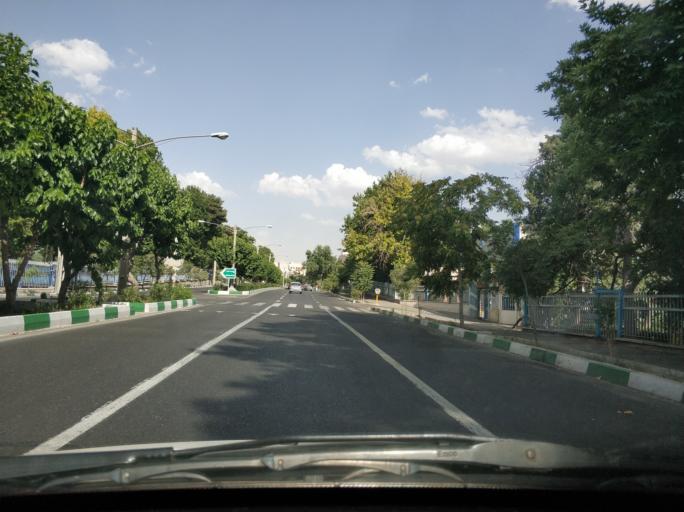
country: IR
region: Tehran
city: Tehran
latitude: 35.7429
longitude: 51.5832
